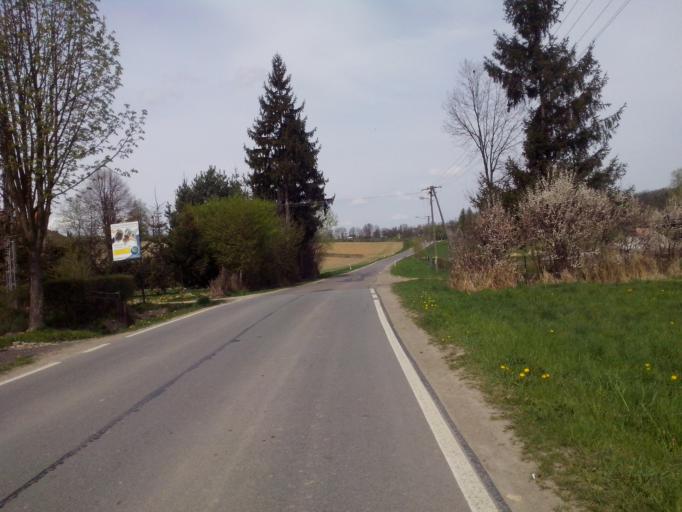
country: PL
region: Subcarpathian Voivodeship
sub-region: Powiat strzyzowski
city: Jawornik
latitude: 49.8122
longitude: 21.8448
